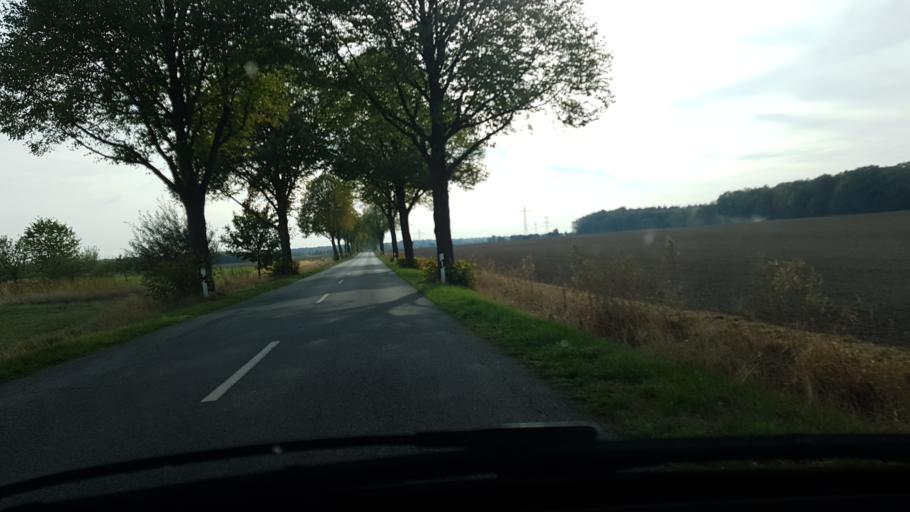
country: DE
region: Lower Saxony
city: Lehre
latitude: 52.3872
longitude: 10.6855
